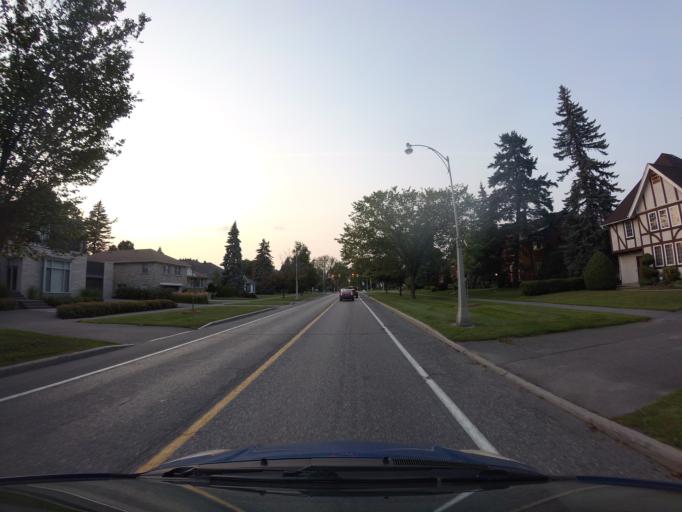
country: CA
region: Ontario
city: Ottawa
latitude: 45.3921
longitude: -75.7389
